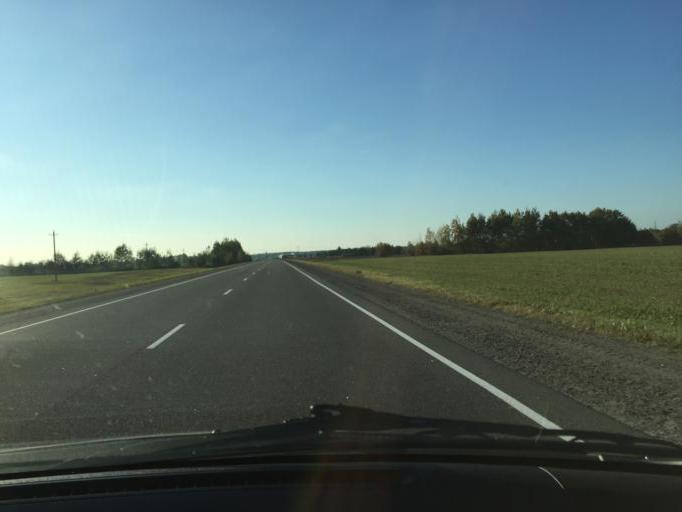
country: BY
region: Brest
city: Horad Luninyets
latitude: 52.3152
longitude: 26.6429
